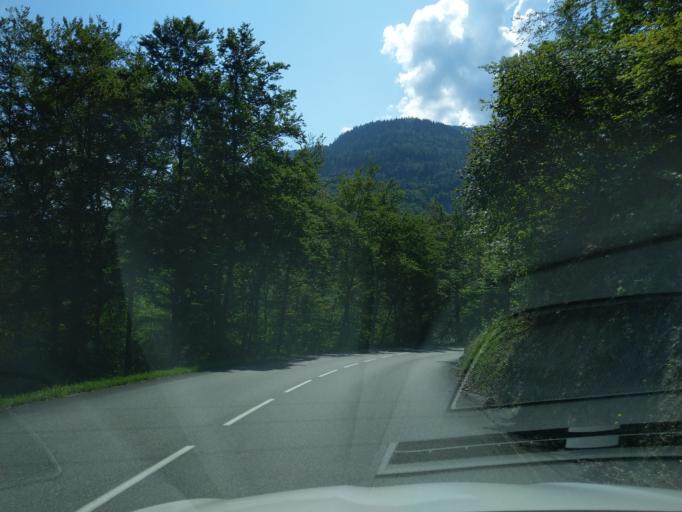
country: FR
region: Rhone-Alpes
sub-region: Departement de la Savoie
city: Les Allues
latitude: 45.4468
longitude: 6.5600
